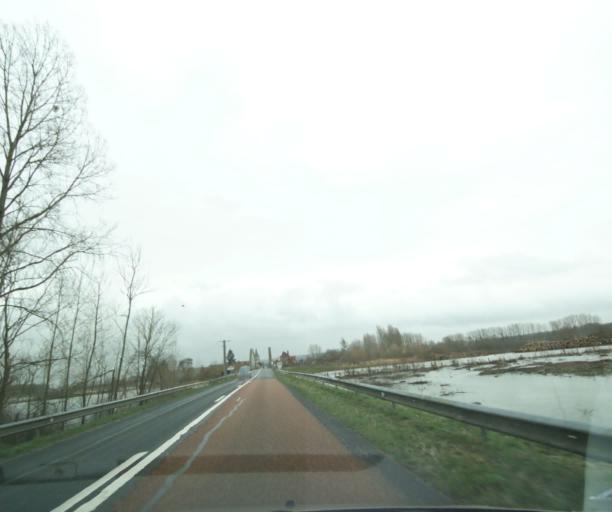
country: FR
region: Picardie
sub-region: Departement de l'Oise
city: Carlepont
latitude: 49.5564
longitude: 3.0425
